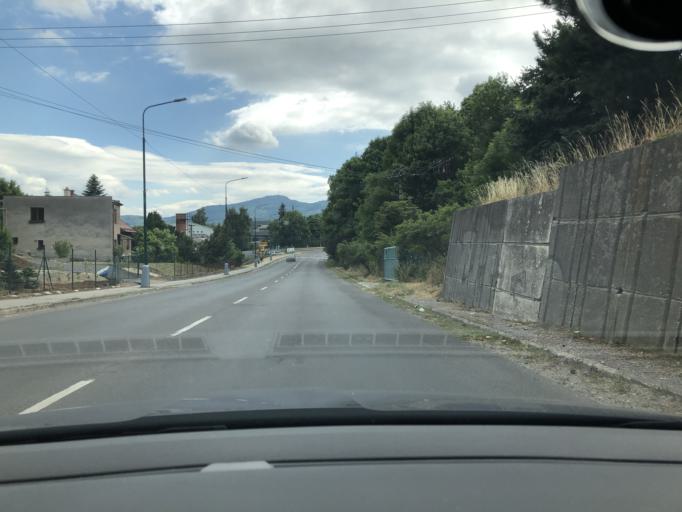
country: SK
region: Banskobystricky
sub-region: Okres Banska Bystrica
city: Banska Stiavnica
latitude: 48.4513
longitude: 18.9127
